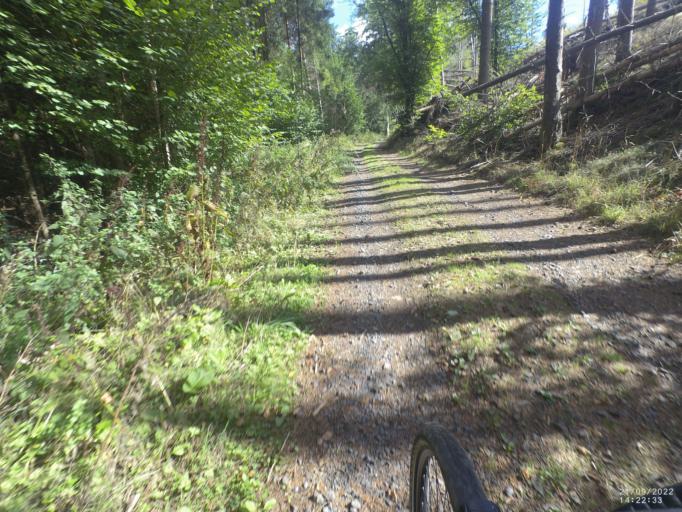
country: DE
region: Rheinland-Pfalz
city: Steiningen
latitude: 50.1786
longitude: 6.9001
